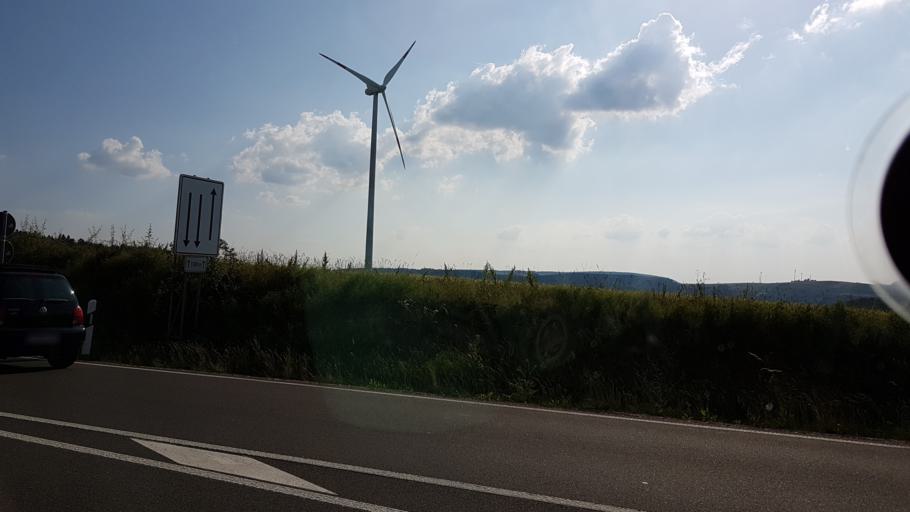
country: DE
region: Rheinland-Pfalz
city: Winterborn
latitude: 49.7665
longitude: 7.8561
